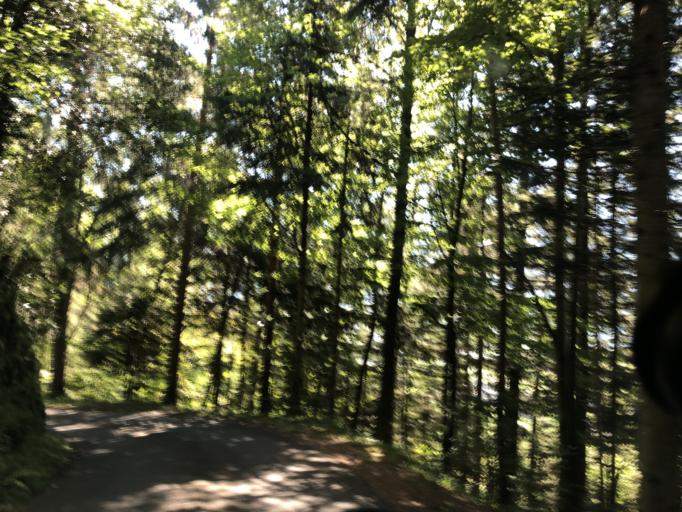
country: CH
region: Uri
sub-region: Uri
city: Altdorf
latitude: 46.8936
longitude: 8.6340
